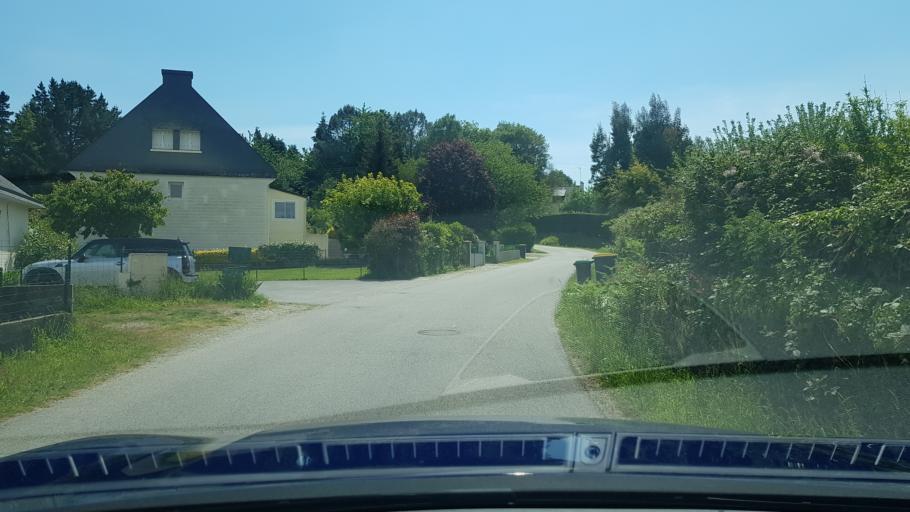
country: FR
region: Brittany
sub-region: Departement du Morbihan
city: Pont-Scorff
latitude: 47.8217
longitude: -3.4121
